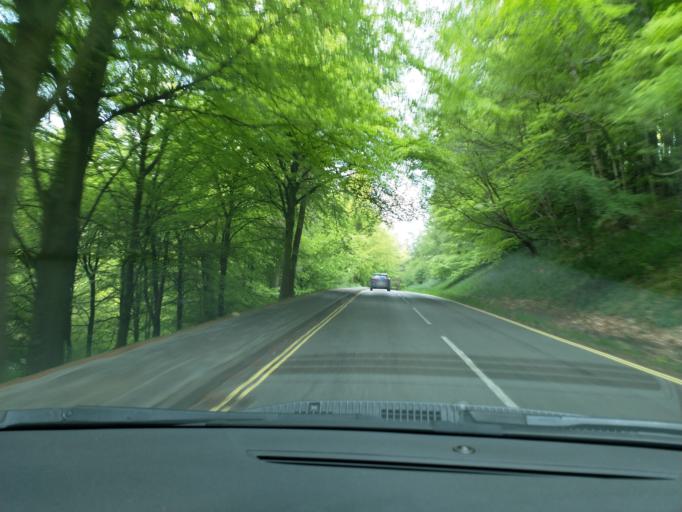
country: GB
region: England
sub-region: Derbyshire
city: Hope Valley
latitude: 53.3884
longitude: -1.7228
